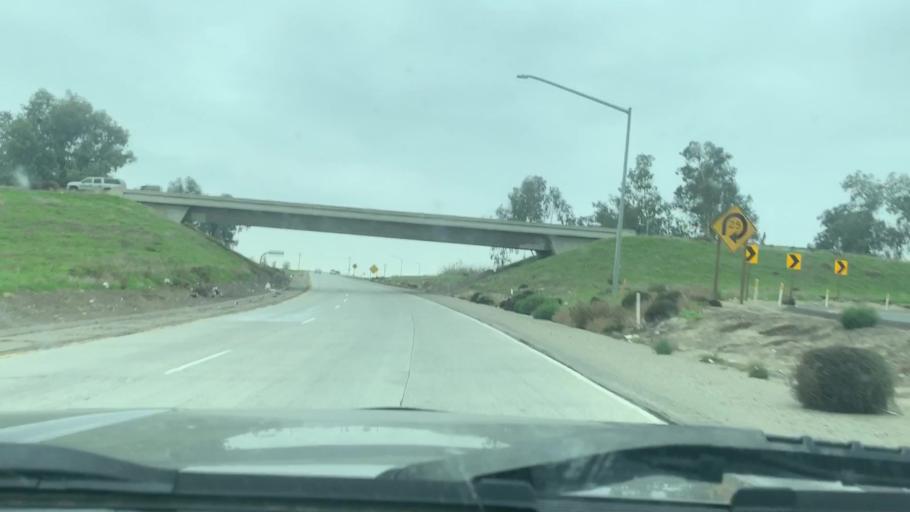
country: US
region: California
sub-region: Tulare County
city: Goshen
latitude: 36.3289
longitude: -119.4104
